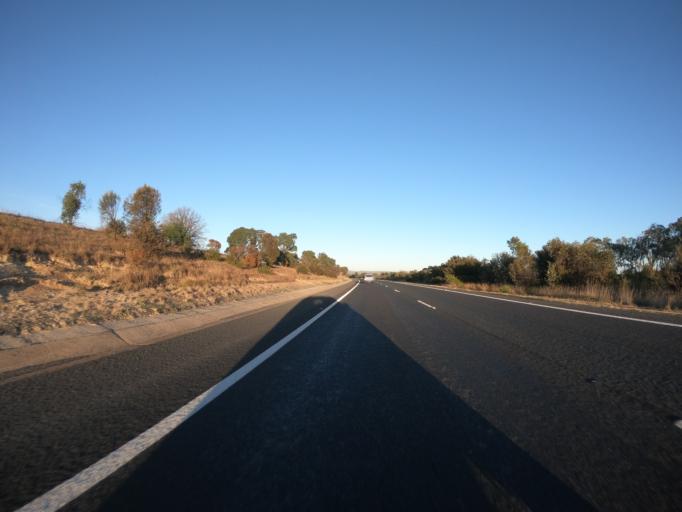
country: AU
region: New South Wales
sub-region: Goulburn Mulwaree
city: Goulburn
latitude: -34.8949
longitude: 149.5000
